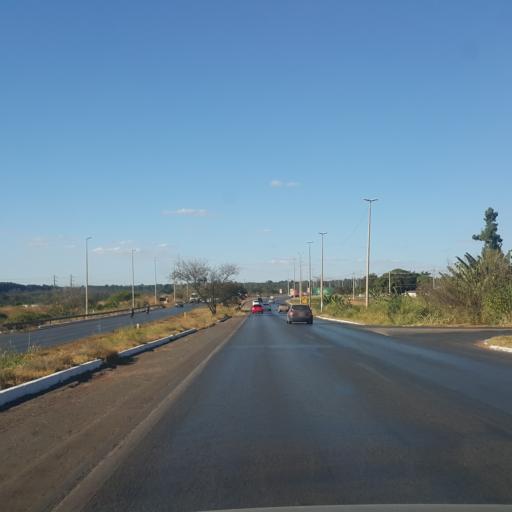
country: BR
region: Federal District
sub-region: Brasilia
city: Brasilia
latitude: -15.8005
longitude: -48.0769
